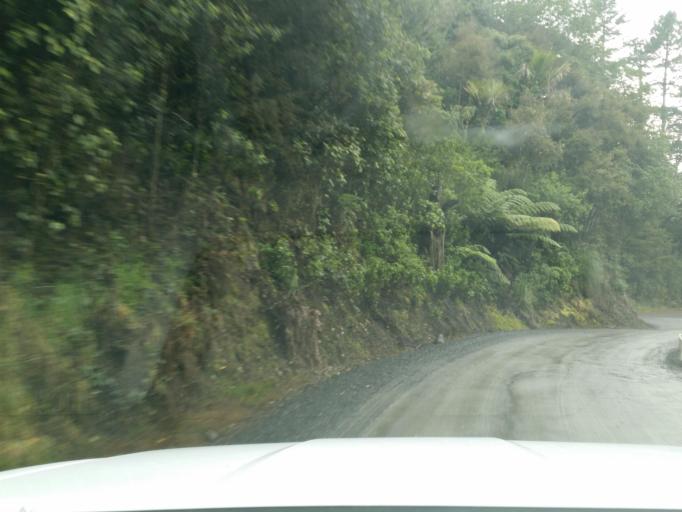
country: NZ
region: Northland
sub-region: Kaipara District
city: Dargaville
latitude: -35.8290
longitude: 173.8273
